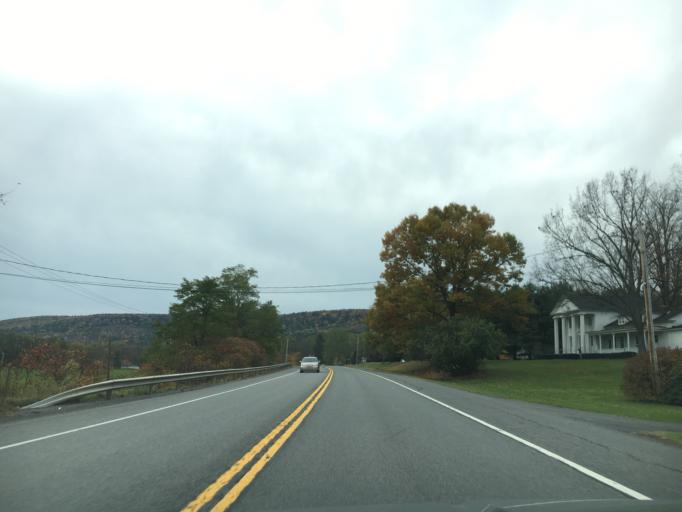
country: US
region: New York
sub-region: Otsego County
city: Oneonta
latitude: 42.5231
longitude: -74.9897
